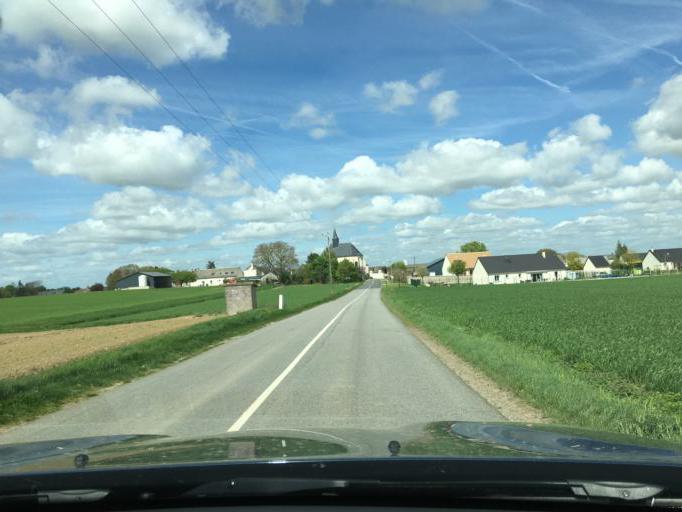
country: FR
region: Centre
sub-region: Departement du Loiret
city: Bricy
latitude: 48.0168
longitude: 1.7982
